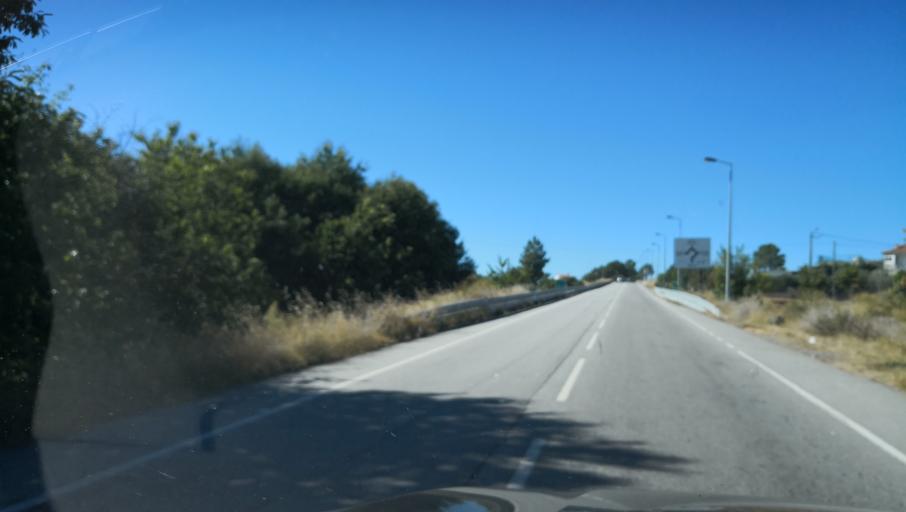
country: PT
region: Vila Real
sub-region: Valpacos
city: Valpacos
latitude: 41.6588
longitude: -7.3256
